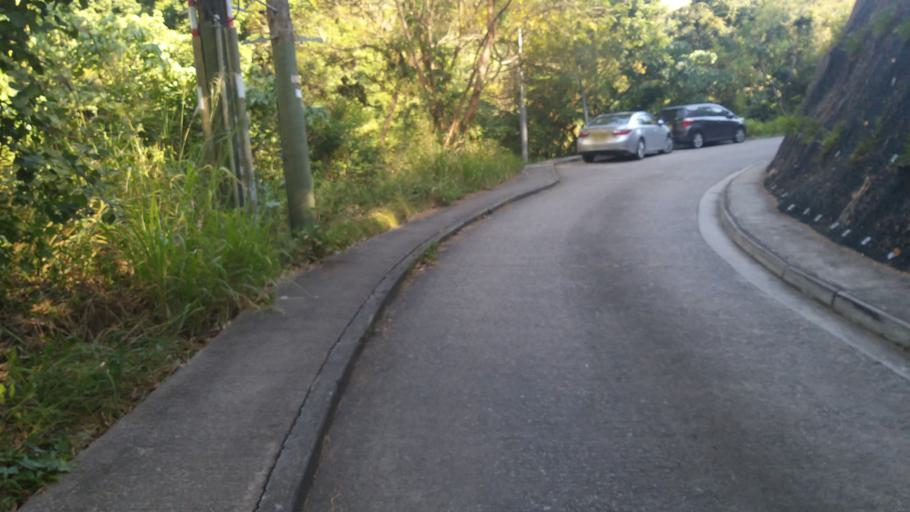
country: HK
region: Tuen Mun
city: Tuen Mun
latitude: 22.4081
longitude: 113.9846
